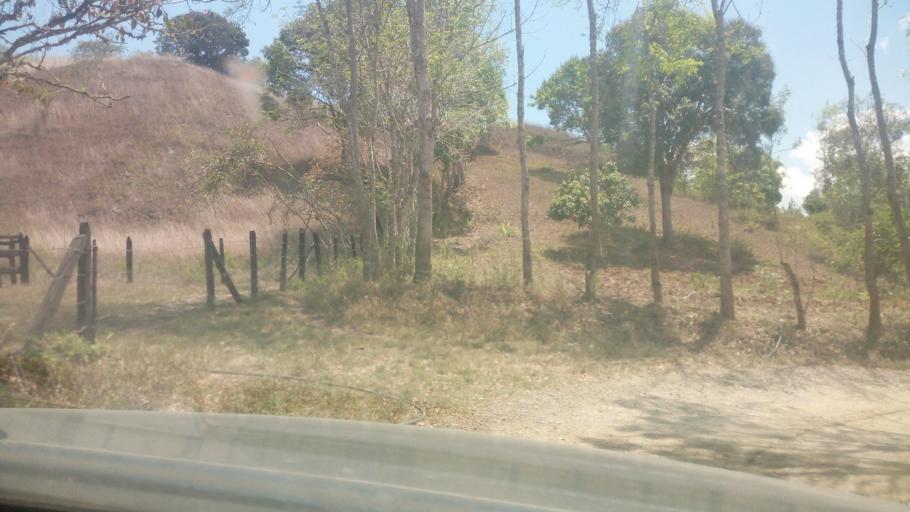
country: CO
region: Boyaca
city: Guateque
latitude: 4.9893
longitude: -73.4614
